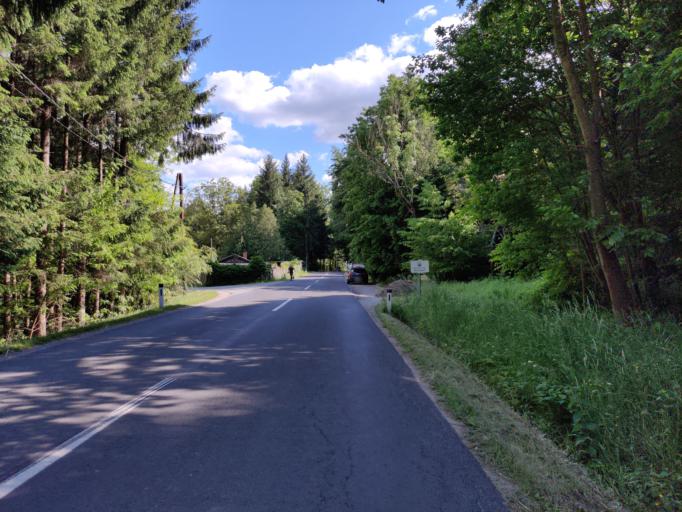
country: AT
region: Styria
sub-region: Politischer Bezirk Graz-Umgebung
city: Thal
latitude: 47.0479
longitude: 15.3616
